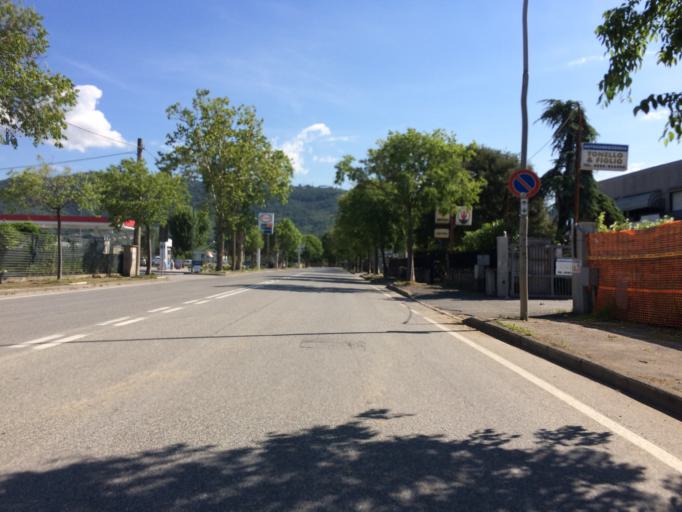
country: IT
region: Tuscany
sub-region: Provincia di Massa-Carrara
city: Marina di Carrara
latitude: 44.0545
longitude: 10.0427
